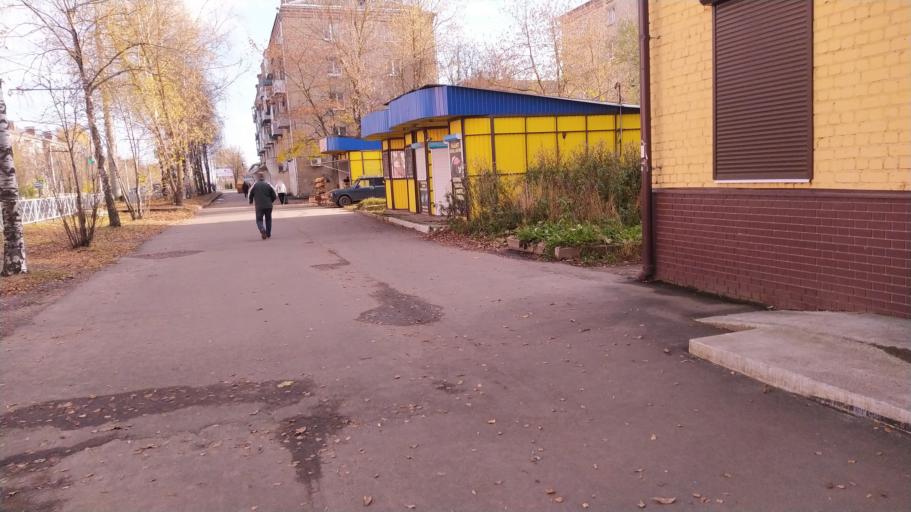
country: RU
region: Jaroslavl
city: Rybinsk
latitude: 58.0570
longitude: 38.7864
